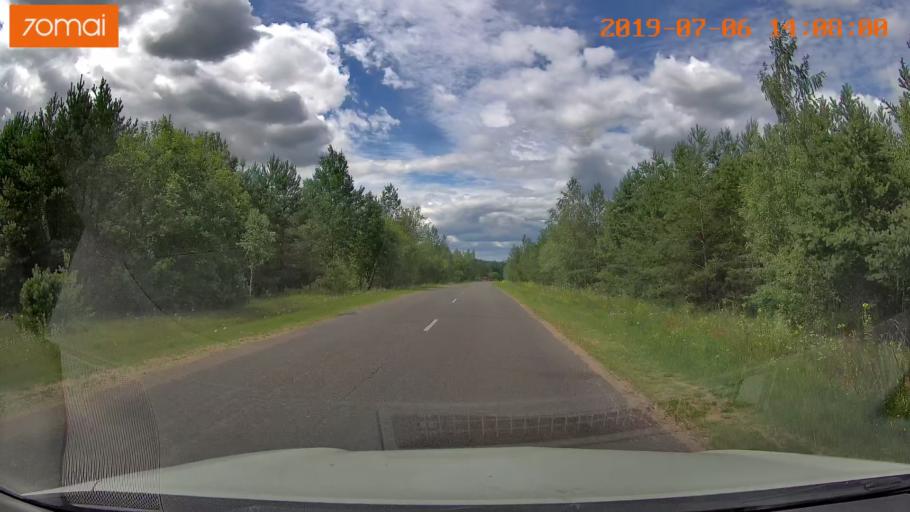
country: BY
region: Minsk
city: Ivyanyets
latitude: 53.8718
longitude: 26.7630
